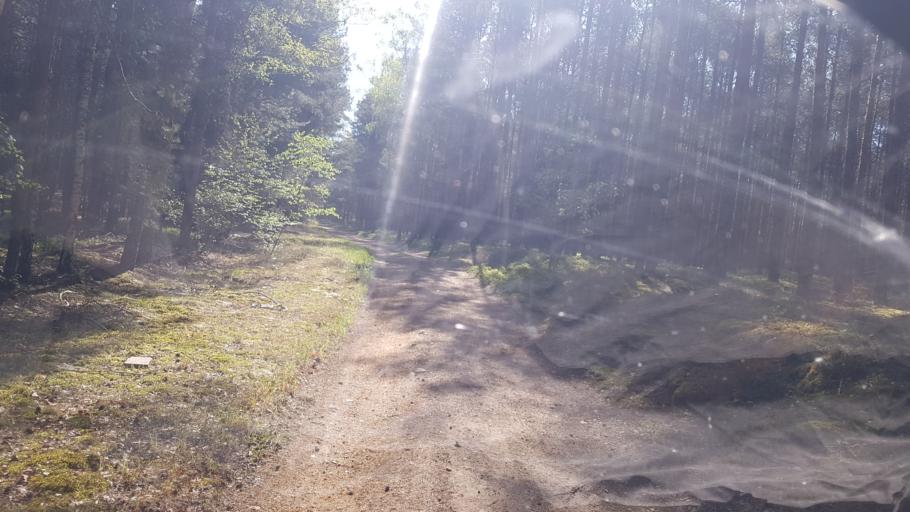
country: DE
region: Brandenburg
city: Crinitz
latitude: 51.7365
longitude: 13.7768
